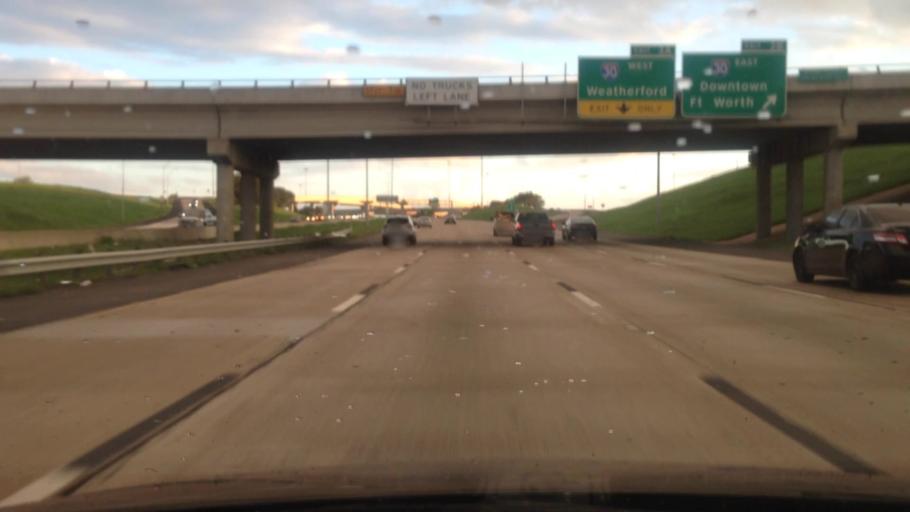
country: US
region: Texas
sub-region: Tarrant County
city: White Settlement
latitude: 32.7445
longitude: -97.4811
